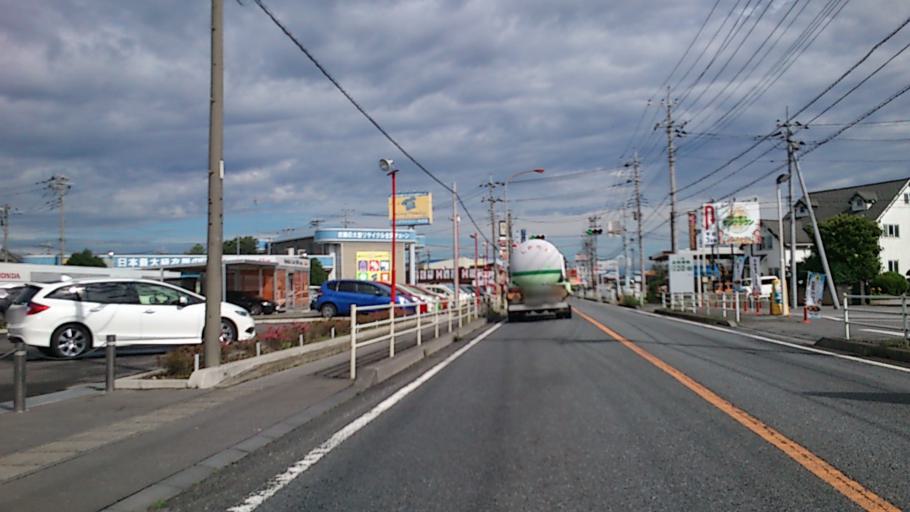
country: JP
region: Saitama
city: Honjo
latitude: 36.2388
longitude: 139.2047
